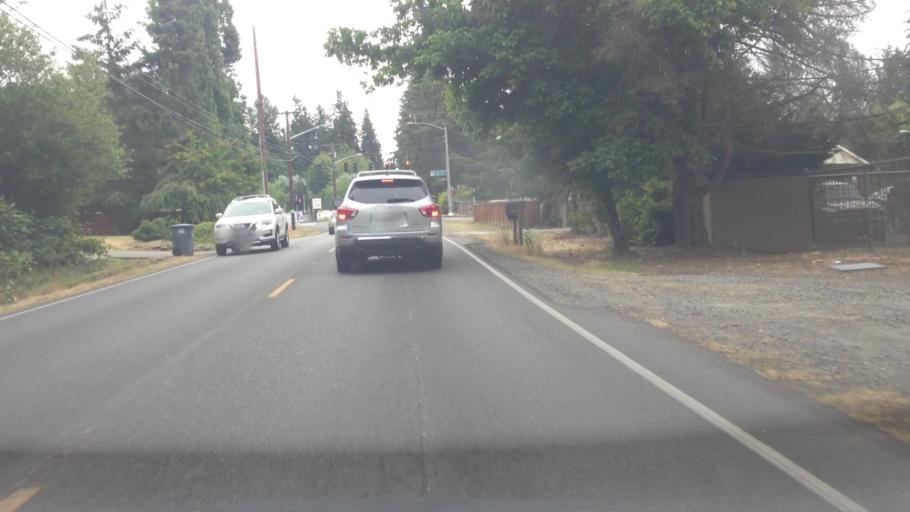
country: US
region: Washington
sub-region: Pierce County
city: South Hill
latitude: 47.1266
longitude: -122.3040
